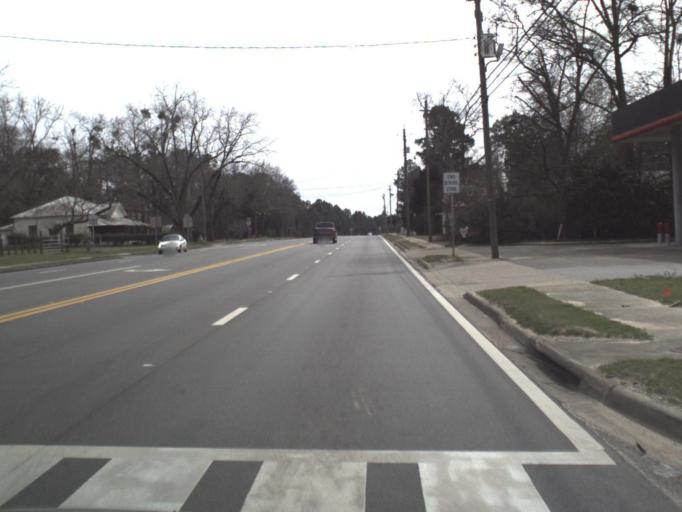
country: US
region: Florida
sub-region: Bay County
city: Youngstown
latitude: 30.3667
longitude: -85.4383
